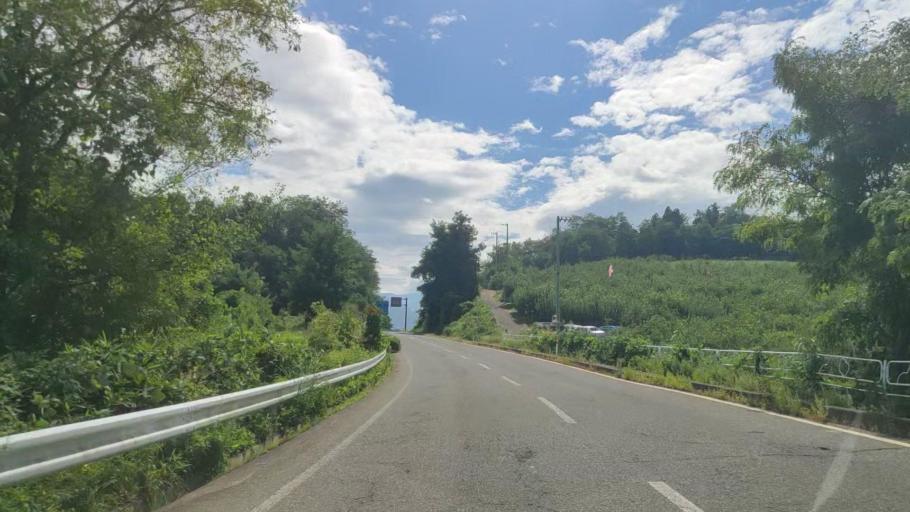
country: JP
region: Nagano
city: Nakano
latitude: 36.7360
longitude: 138.3053
